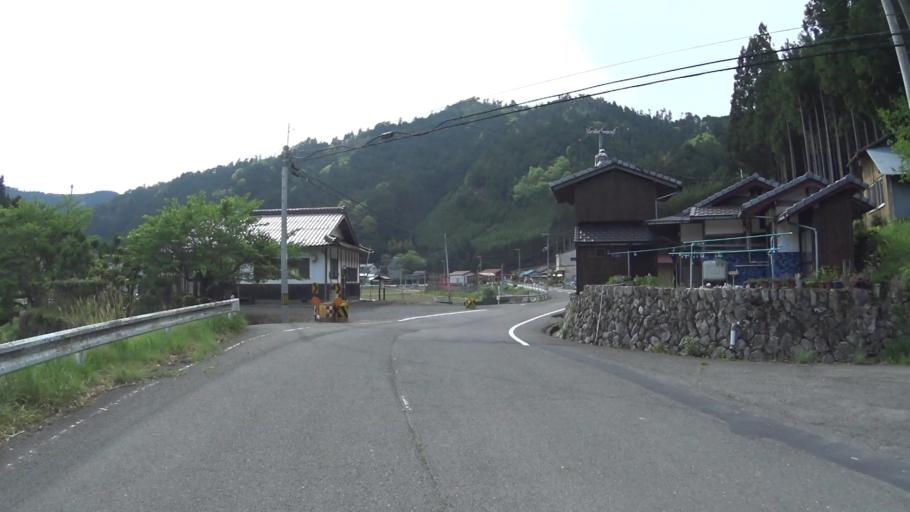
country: JP
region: Kyoto
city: Kameoka
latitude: 35.1230
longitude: 135.6045
